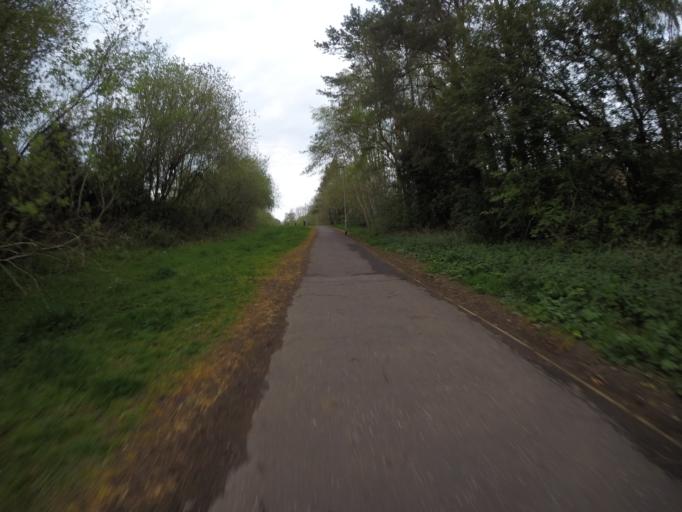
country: GB
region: Scotland
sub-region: North Ayrshire
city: Irvine
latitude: 55.6352
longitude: -4.6366
